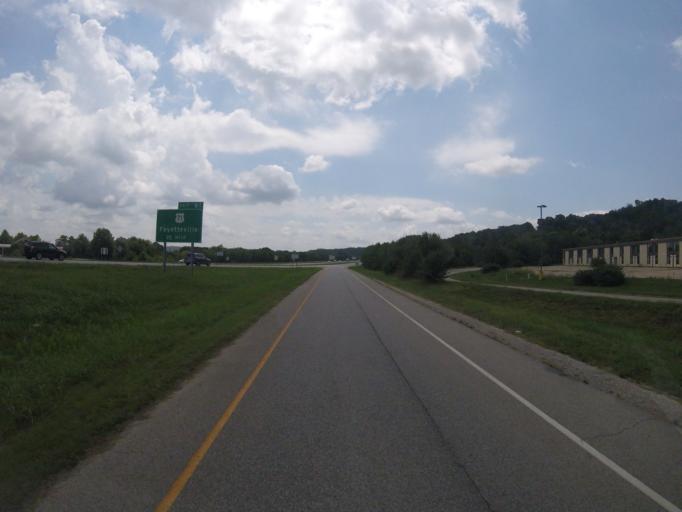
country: US
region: Arkansas
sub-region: Washington County
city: Fayetteville
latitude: 36.0522
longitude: -94.1942
